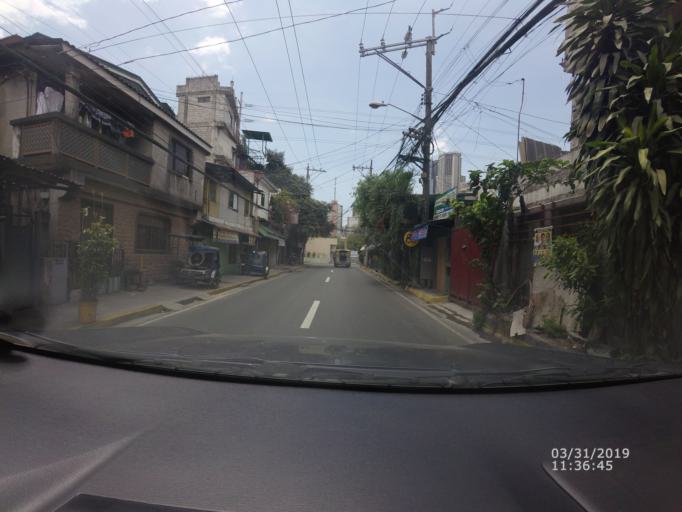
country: PH
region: Metro Manila
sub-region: Mandaluyong
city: Mandaluyong City
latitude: 14.5685
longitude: 121.0341
